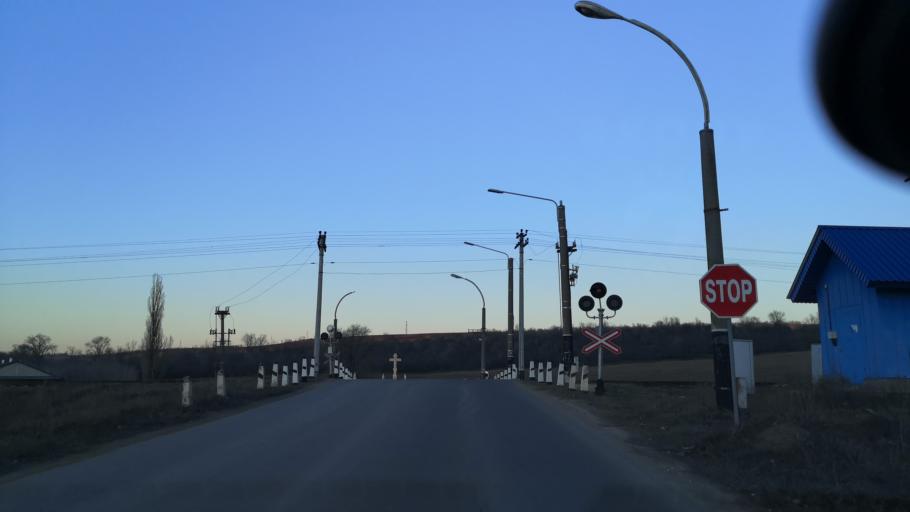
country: MD
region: Anenii Noi
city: Anenii Noi
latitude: 46.8905
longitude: 29.2413
